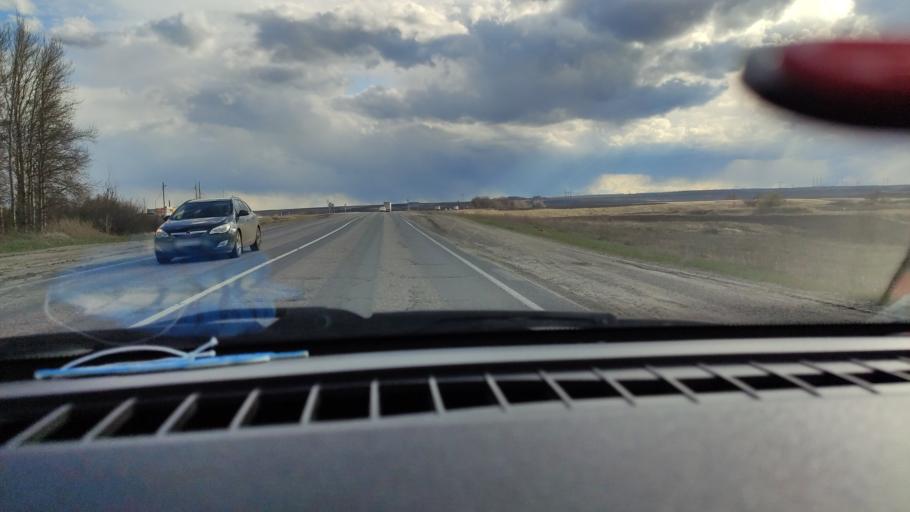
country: RU
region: Saratov
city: Sinodskoye
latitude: 51.9721
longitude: 46.6436
